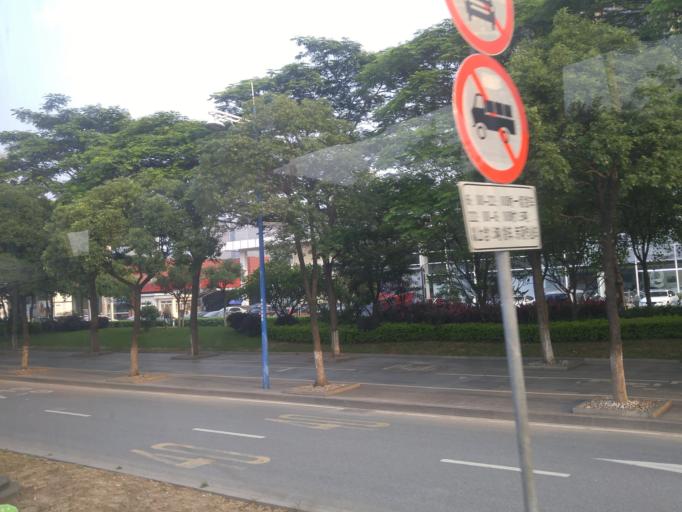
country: CN
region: Guangdong
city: Foshan
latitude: 23.0699
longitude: 113.1389
